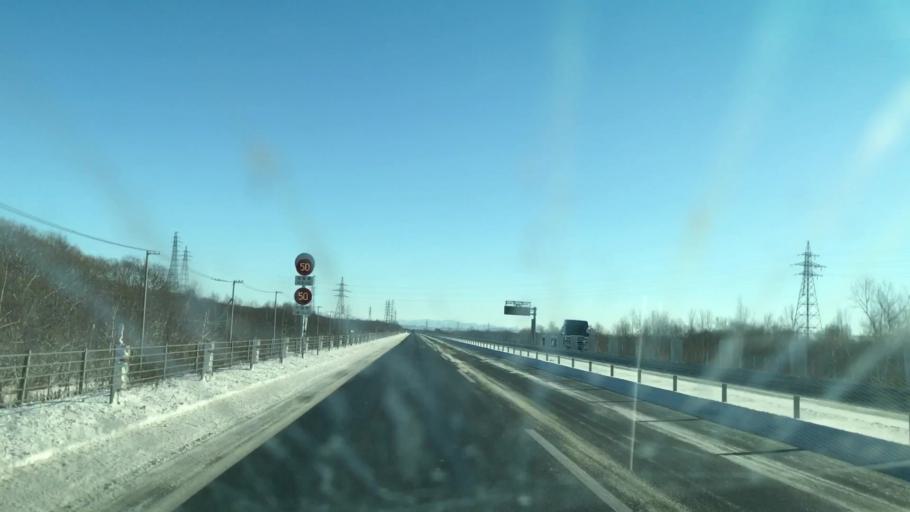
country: JP
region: Hokkaido
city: Tomakomai
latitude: 42.6735
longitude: 141.7585
